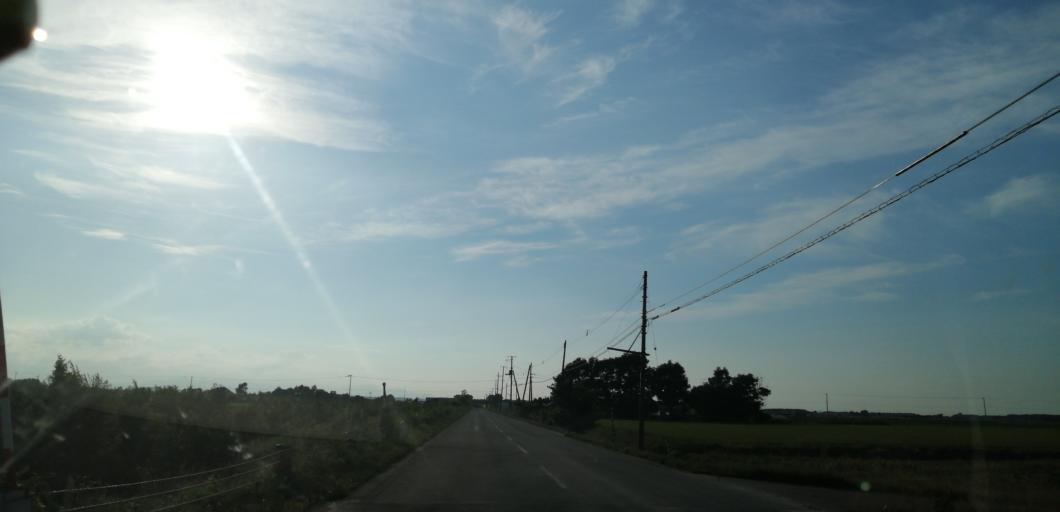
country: JP
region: Hokkaido
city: Kitahiroshima
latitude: 42.9591
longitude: 141.6463
